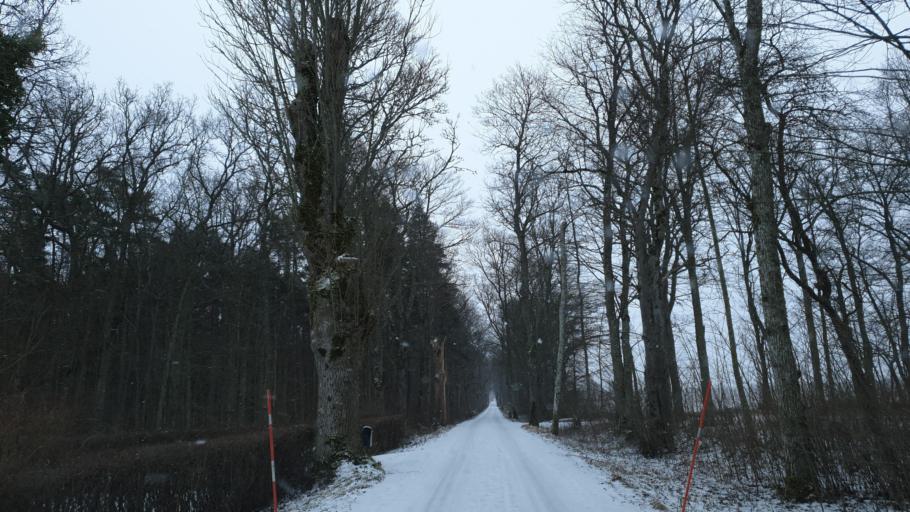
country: SE
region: Gotland
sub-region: Gotland
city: Visby
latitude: 57.5236
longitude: 18.4487
